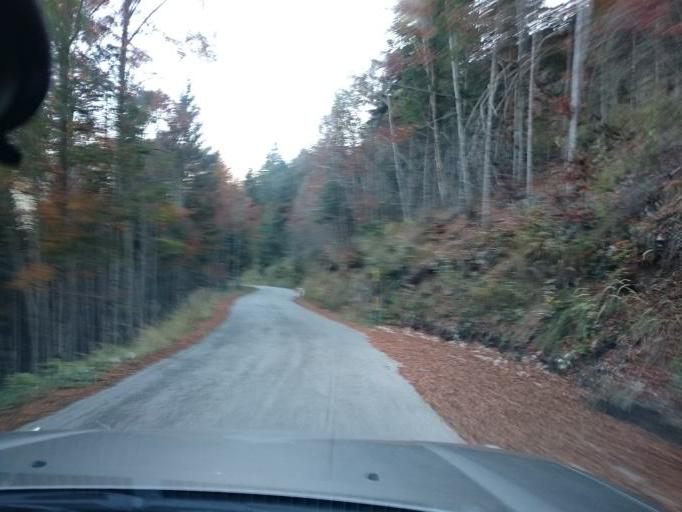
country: IT
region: Veneto
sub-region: Provincia di Vicenza
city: Roana
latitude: 45.9585
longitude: 11.4242
